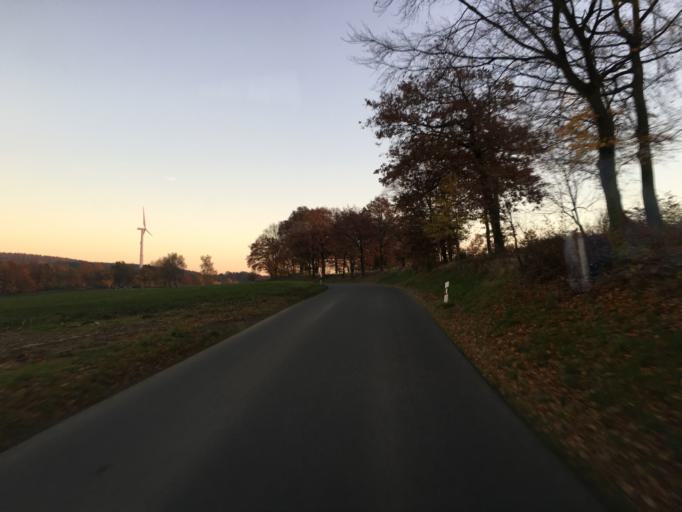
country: DE
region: North Rhine-Westphalia
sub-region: Regierungsbezirk Arnsberg
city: Nachrodt-Wiblingwerde
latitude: 51.2742
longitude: 7.5955
